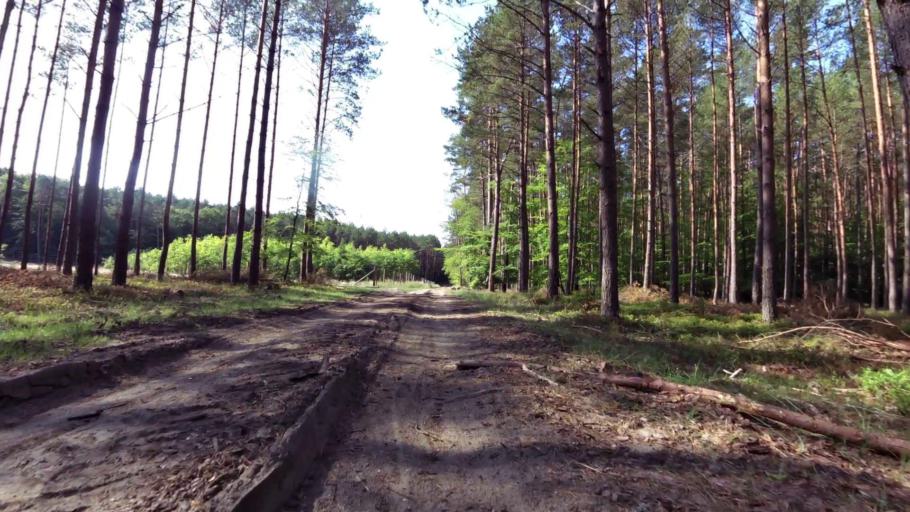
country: PL
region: West Pomeranian Voivodeship
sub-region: Powiat kamienski
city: Miedzyzdroje
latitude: 53.9172
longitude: 14.4995
